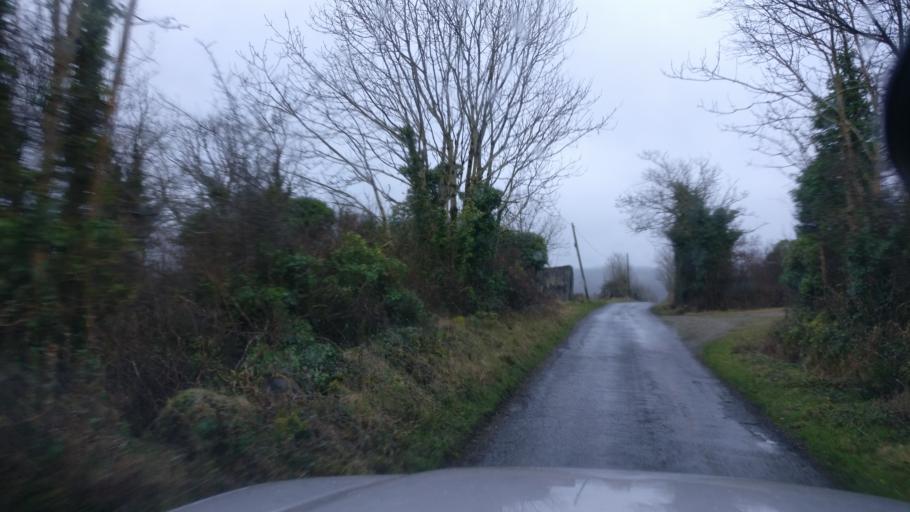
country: IE
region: Connaught
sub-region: County Galway
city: Loughrea
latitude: 53.1567
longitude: -8.6376
